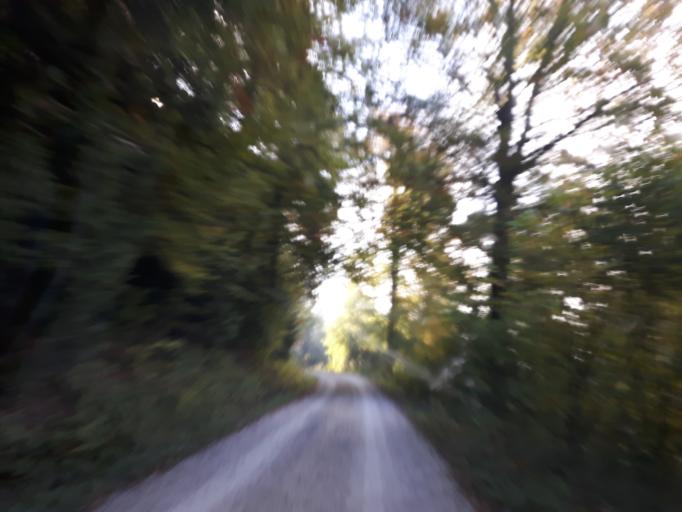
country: CH
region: Bern
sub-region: Oberaargau
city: Roggwil
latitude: 47.2417
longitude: 7.8344
